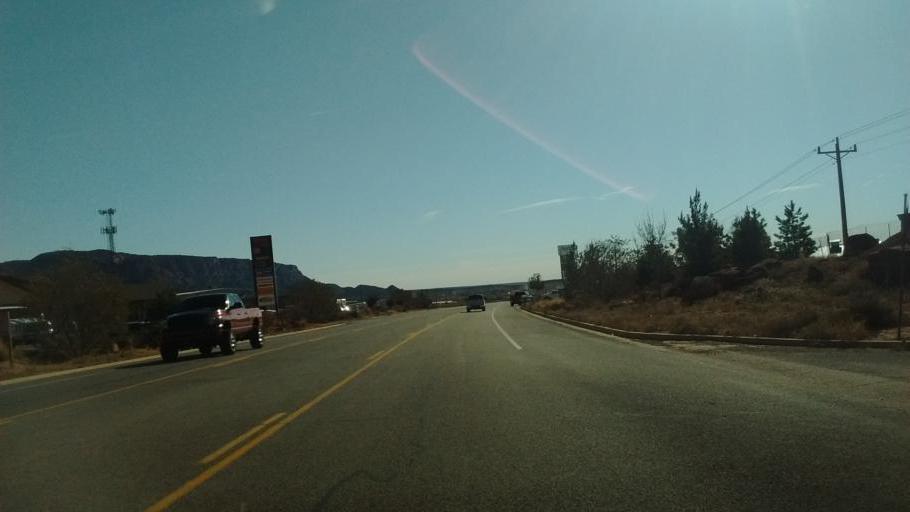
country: US
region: Arizona
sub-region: Mohave County
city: Colorado City
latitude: 37.0018
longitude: -113.0003
